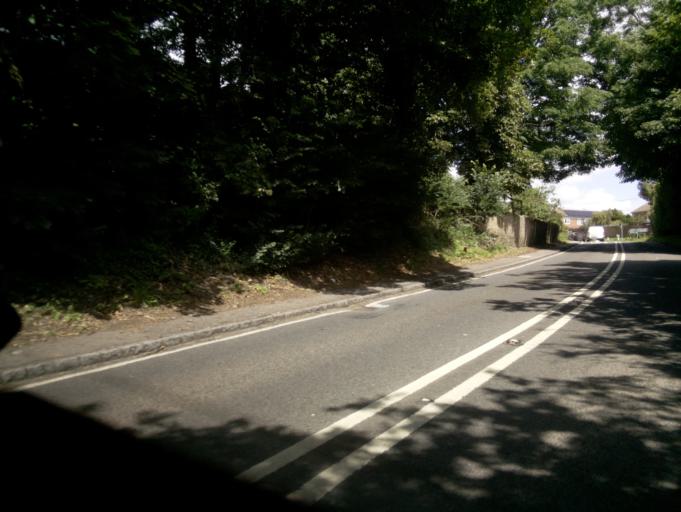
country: GB
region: England
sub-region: Buckinghamshire
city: Aylesbury
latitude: 51.8759
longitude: -0.8317
